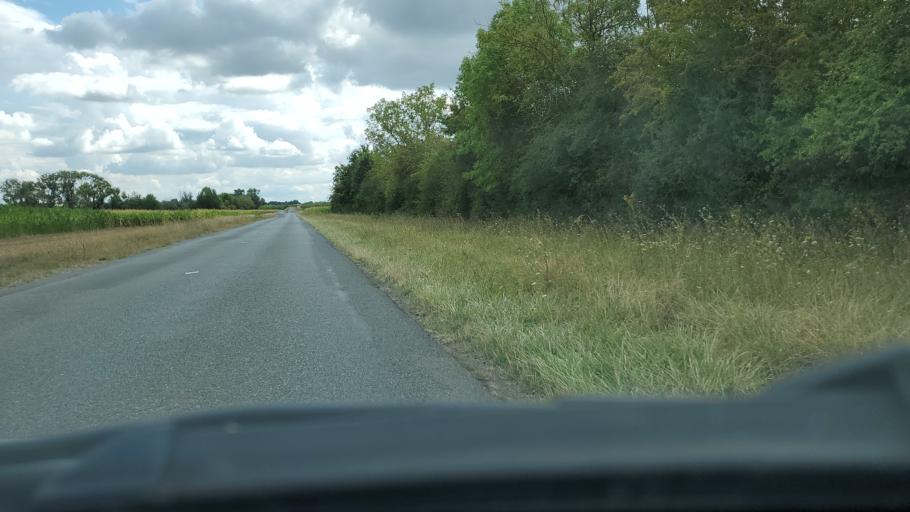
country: FR
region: Ile-de-France
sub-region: Departement de Seine-et-Marne
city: Pommeuse
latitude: 48.8530
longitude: 3.0185
